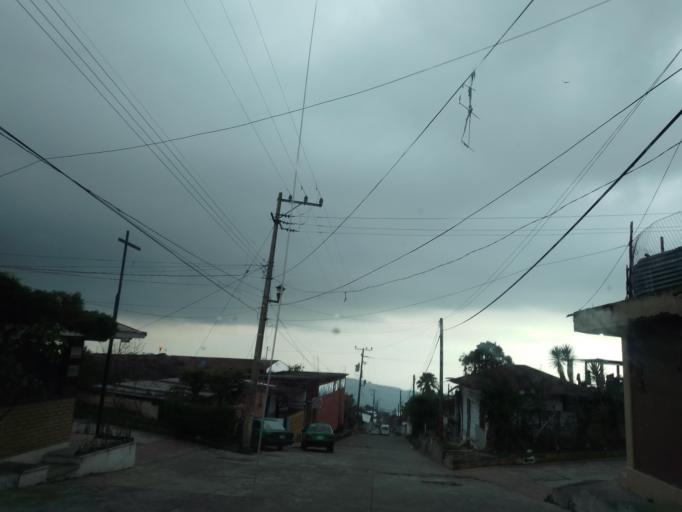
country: MX
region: Chiapas
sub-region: Union Juarez
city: Santo Domingo
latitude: 15.0636
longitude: -92.0812
